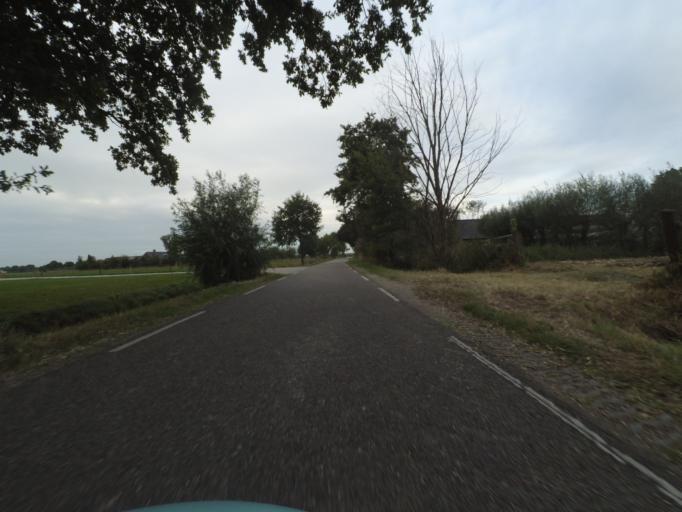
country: NL
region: Utrecht
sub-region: Gemeente Wijk bij Duurstede
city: Wijk bij Duurstede
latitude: 51.9922
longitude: 5.3385
